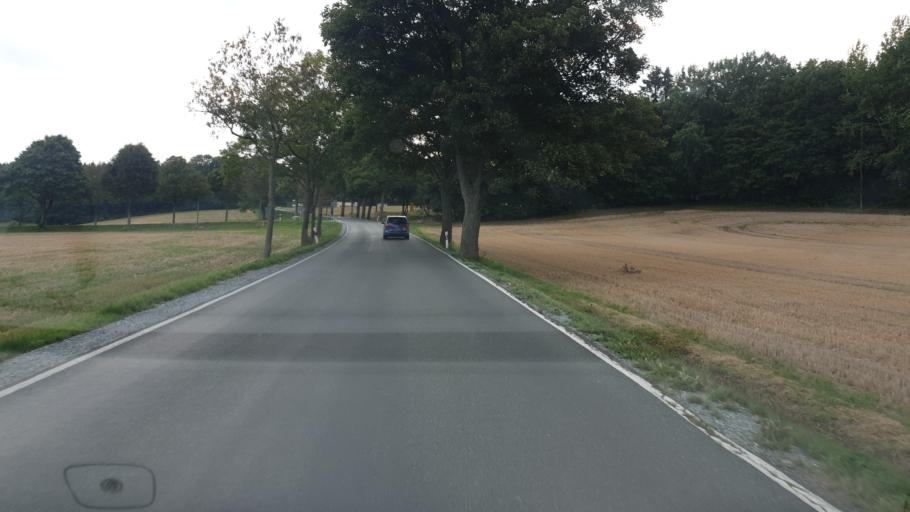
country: DE
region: Saxony
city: Wiesa
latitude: 50.6407
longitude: 13.0071
